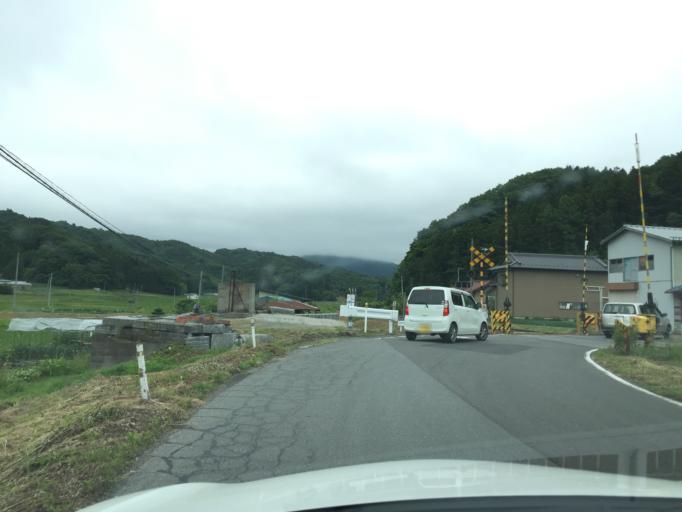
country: JP
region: Fukushima
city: Funehikimachi-funehiki
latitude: 37.3484
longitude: 140.6483
